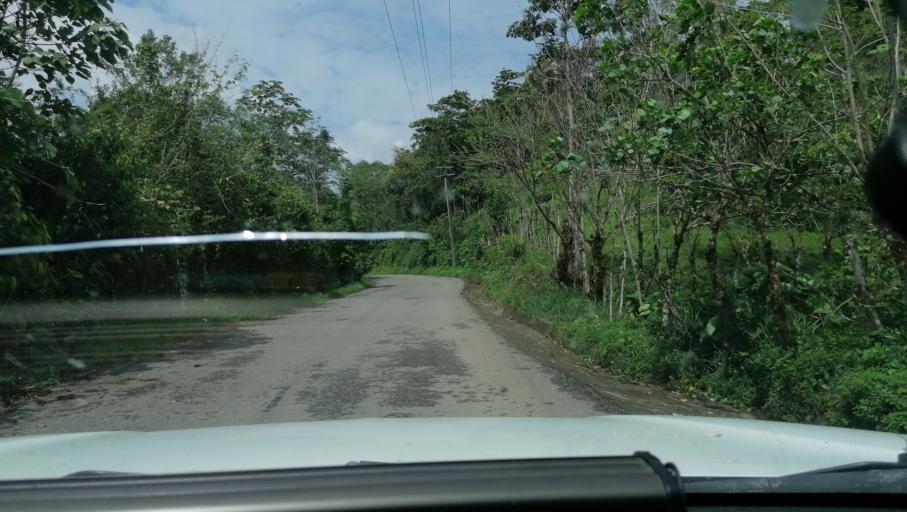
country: MX
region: Chiapas
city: Ocotepec
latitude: 17.3201
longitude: -93.1689
